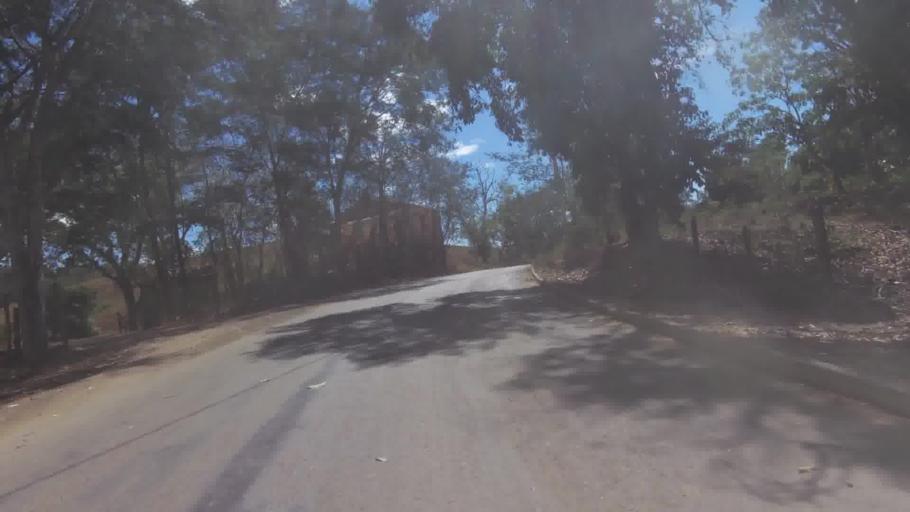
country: BR
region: Espirito Santo
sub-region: Cachoeiro De Itapemirim
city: Cachoeiro de Itapemirim
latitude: -20.9325
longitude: -41.2146
